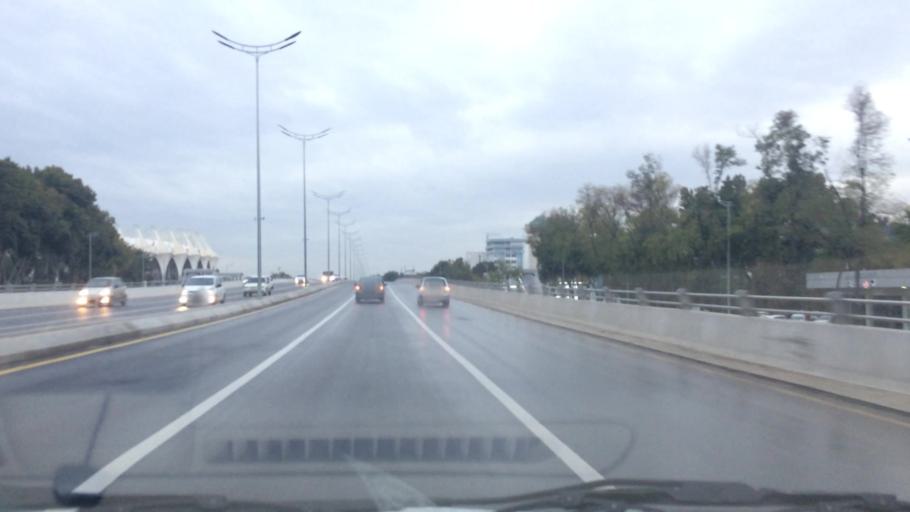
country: UZ
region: Toshkent Shahri
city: Tashkent
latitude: 41.2842
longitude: 69.2146
